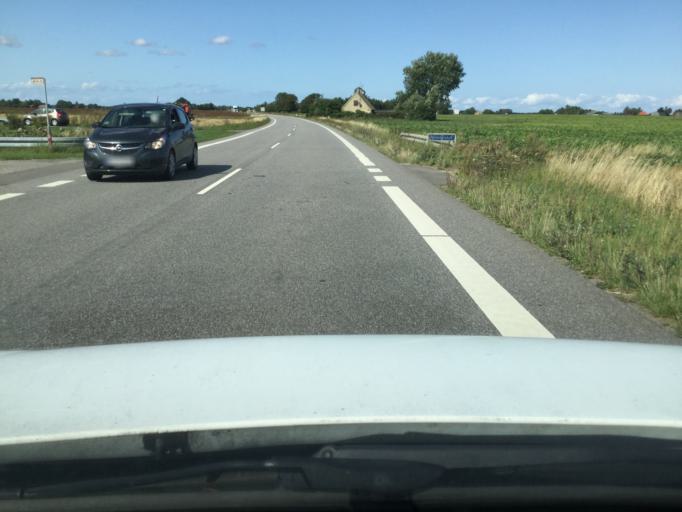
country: DK
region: Zealand
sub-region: Lolland Kommune
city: Rodby
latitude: 54.7415
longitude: 11.3889
